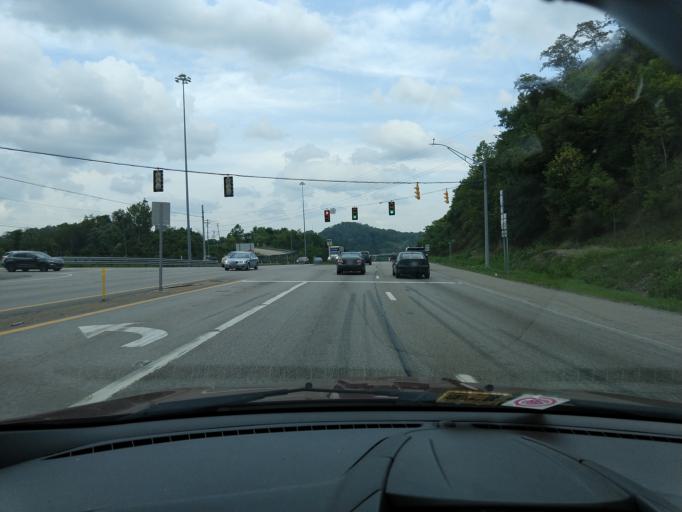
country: US
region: West Virginia
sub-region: Harrison County
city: Despard
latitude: 39.2778
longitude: -80.2938
